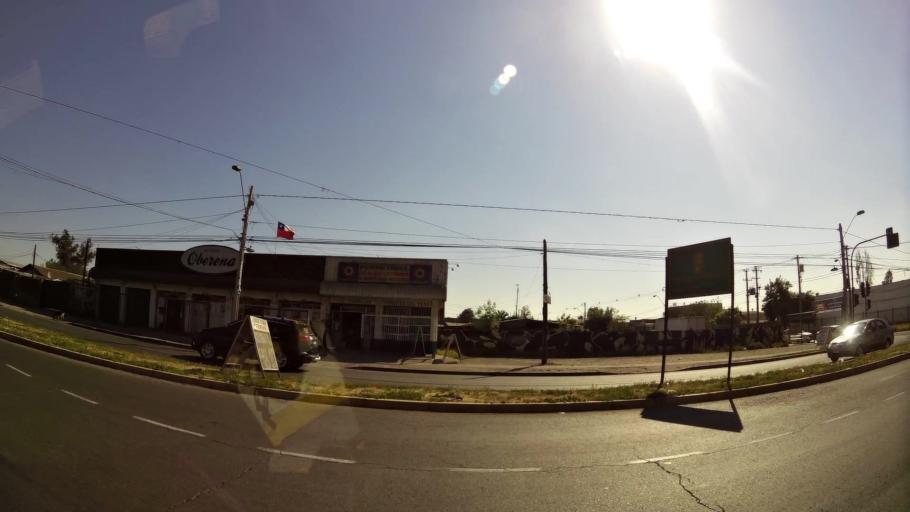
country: CL
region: Santiago Metropolitan
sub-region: Provincia de Santiago
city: La Pintana
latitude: -33.5265
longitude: -70.6097
